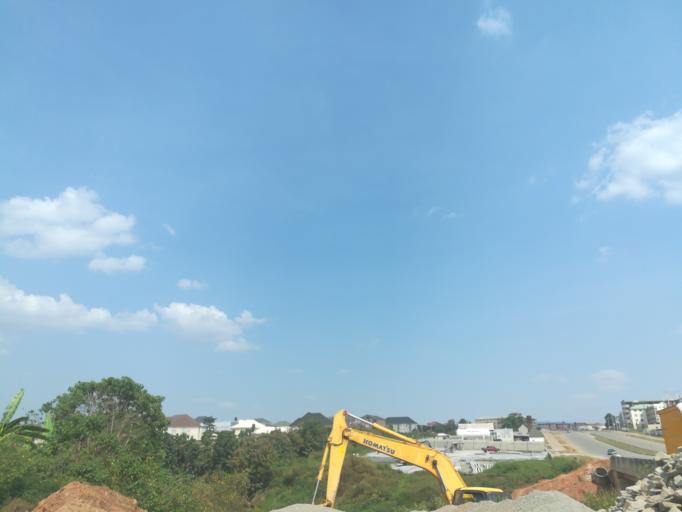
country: NG
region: Abuja Federal Capital Territory
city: Abuja
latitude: 9.0544
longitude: 7.4345
